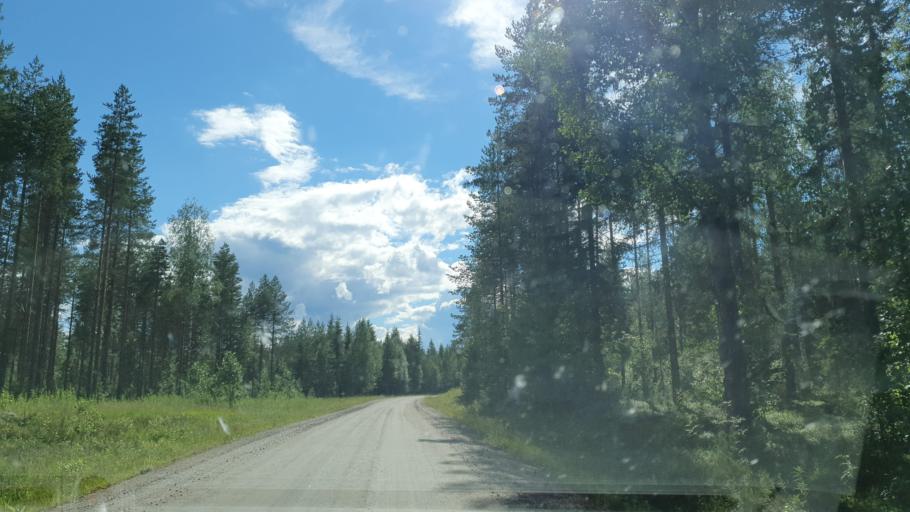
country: FI
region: Kainuu
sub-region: Kehys-Kainuu
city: Kuhmo
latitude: 64.1559
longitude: 29.8058
